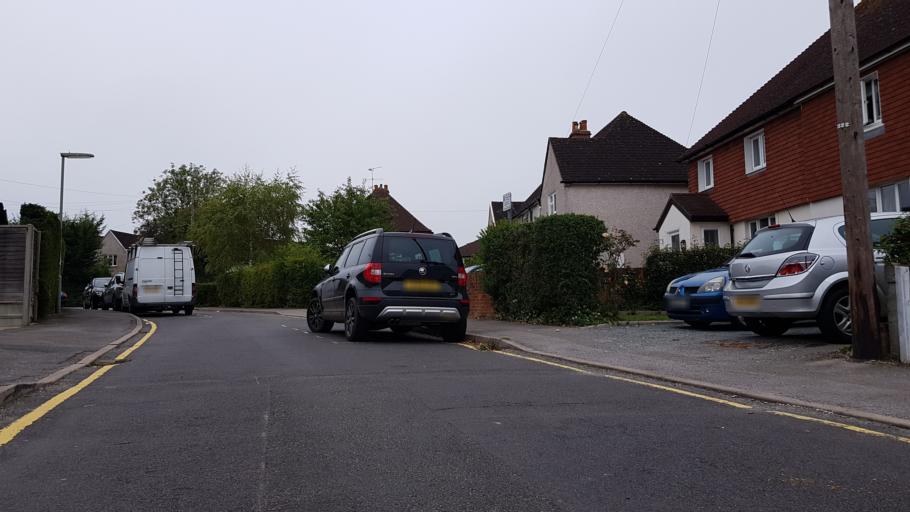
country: GB
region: England
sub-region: Surrey
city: Guildford
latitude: 51.2391
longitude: -0.5919
